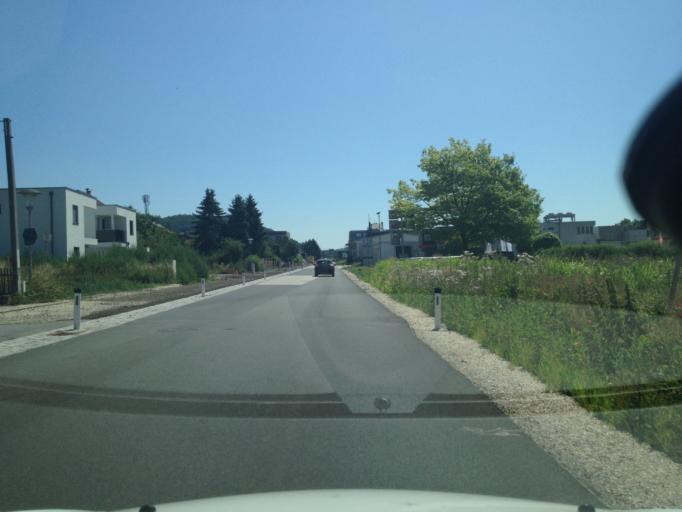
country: AT
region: Upper Austria
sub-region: Politischer Bezirk Urfahr-Umgebung
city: Steyregg
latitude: 48.2843
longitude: 14.3576
